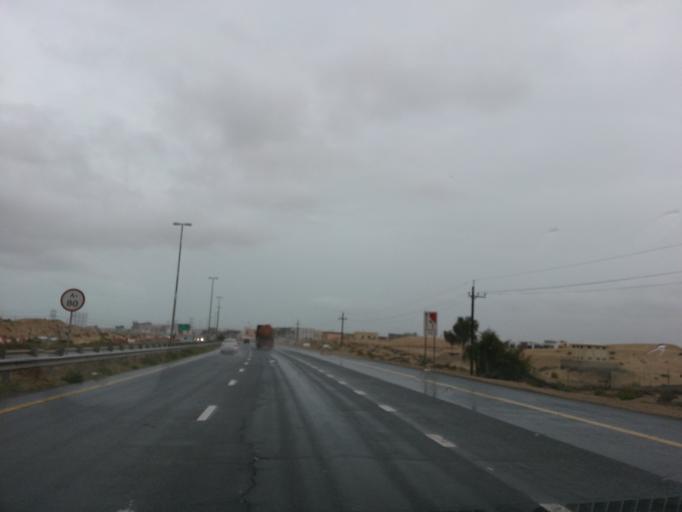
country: AE
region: Dubai
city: Dubai
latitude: 25.0644
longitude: 55.2204
